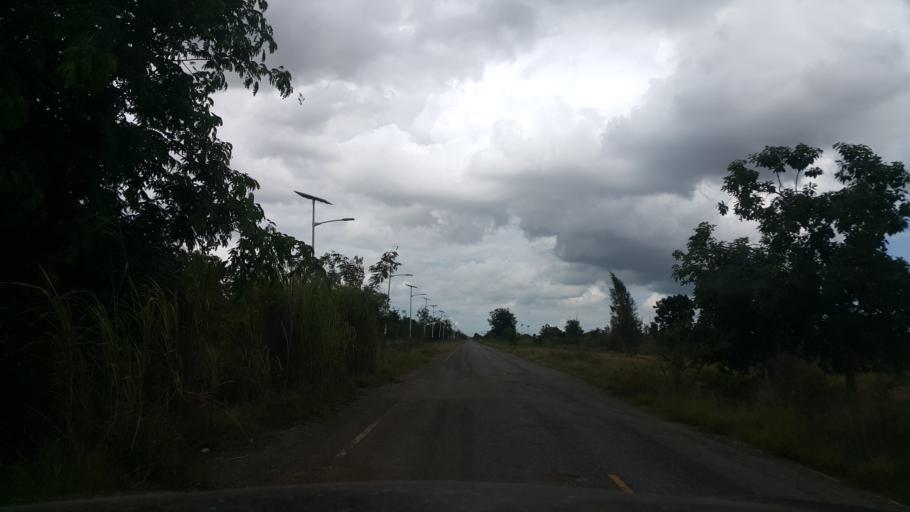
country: TH
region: Sukhothai
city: Ban Na
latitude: 17.0610
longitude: 99.7817
